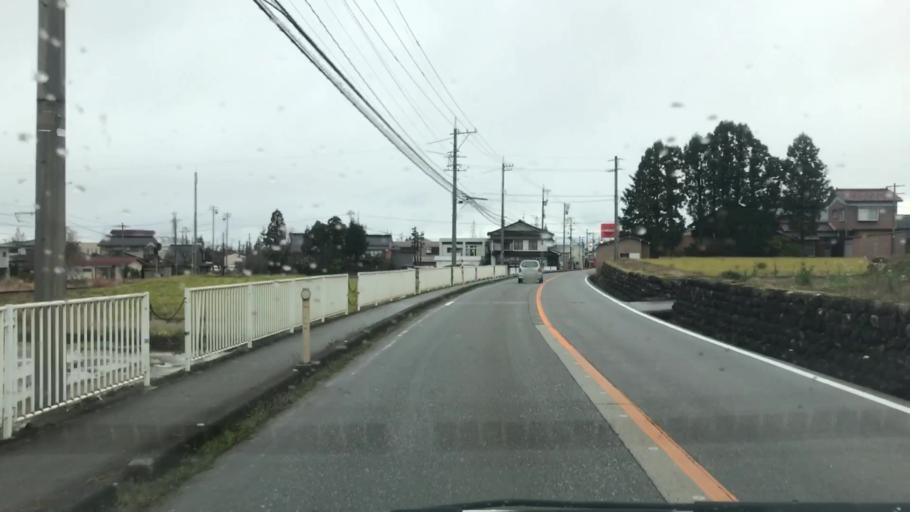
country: JP
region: Toyama
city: Kamiichi
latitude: 36.6053
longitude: 137.3207
